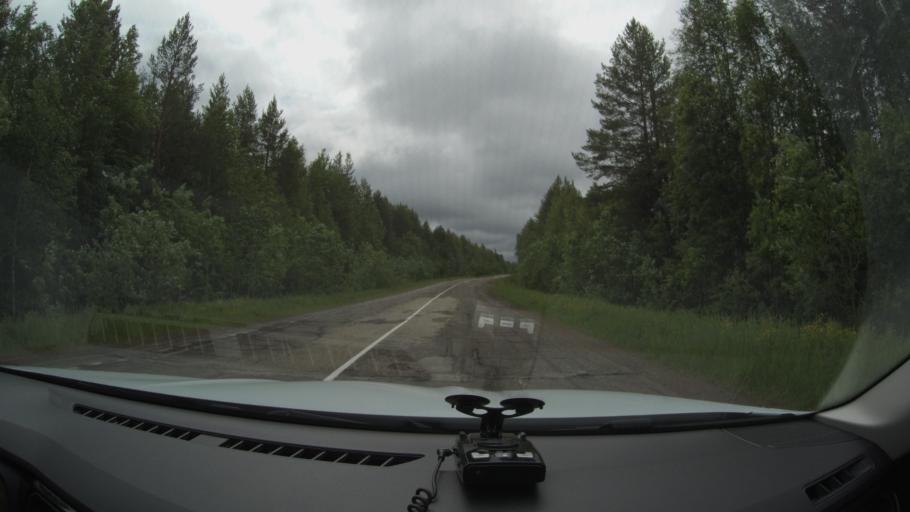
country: RU
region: Komi Republic
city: Nizhniy Odes
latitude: 63.6385
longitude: 54.6441
